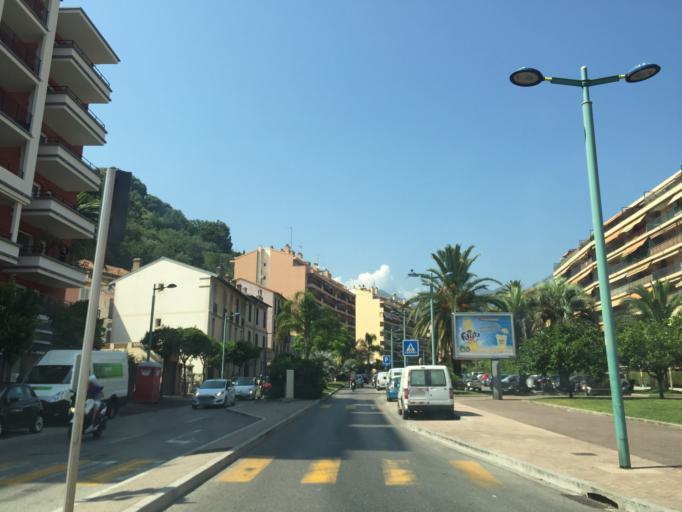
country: FR
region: Provence-Alpes-Cote d'Azur
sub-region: Departement des Alpes-Maritimes
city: Menton
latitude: 43.7779
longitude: 7.4938
